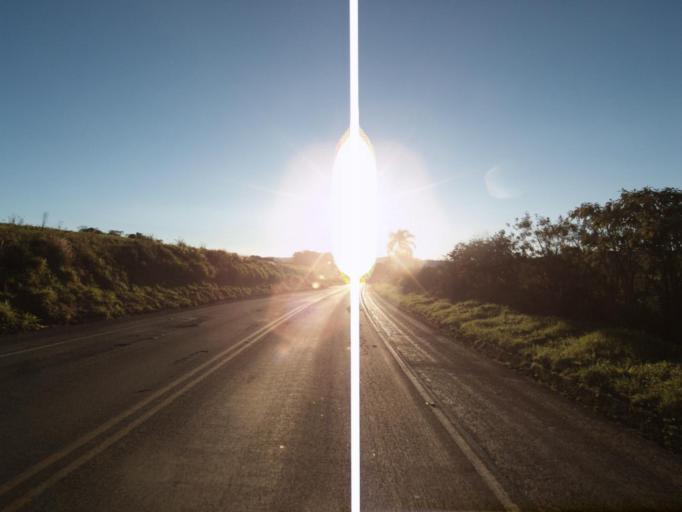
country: BR
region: Santa Catarina
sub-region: Chapeco
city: Chapeco
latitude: -26.8325
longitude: -53.0152
